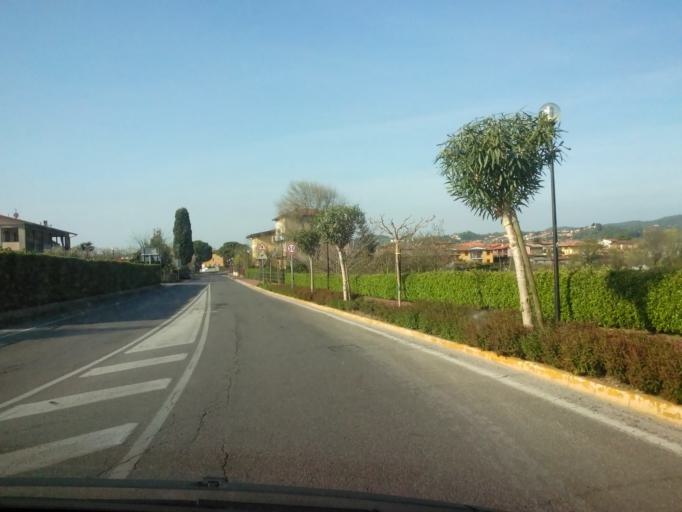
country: IT
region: Lombardy
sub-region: Provincia di Brescia
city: Manerba del Garda
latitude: 45.5494
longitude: 10.5413
